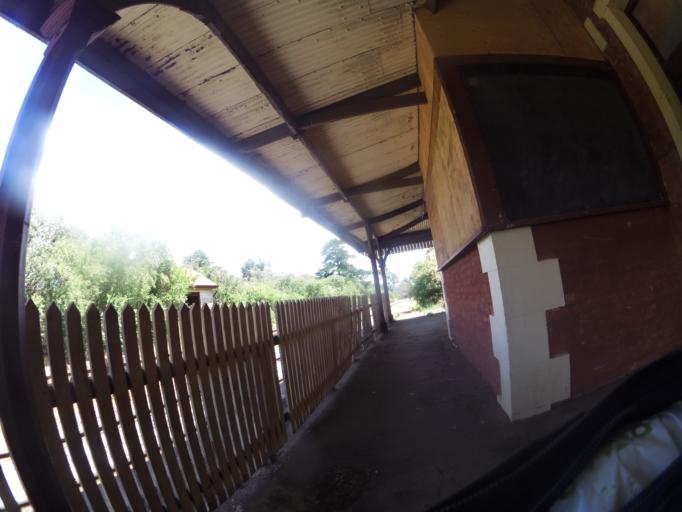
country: AU
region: Victoria
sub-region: Mount Alexander
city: Castlemaine
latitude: -37.0041
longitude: 144.2531
